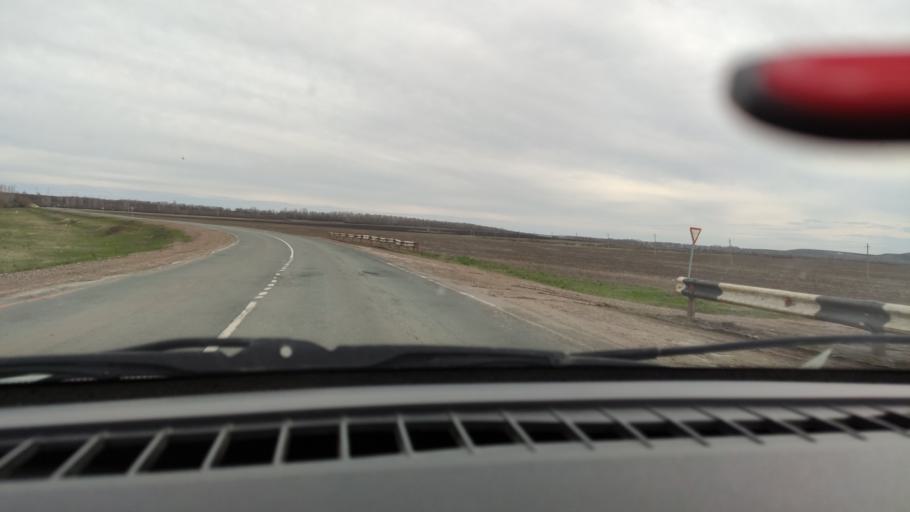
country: RU
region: Bashkortostan
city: Yermolayevo
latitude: 52.4723
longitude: 55.8293
